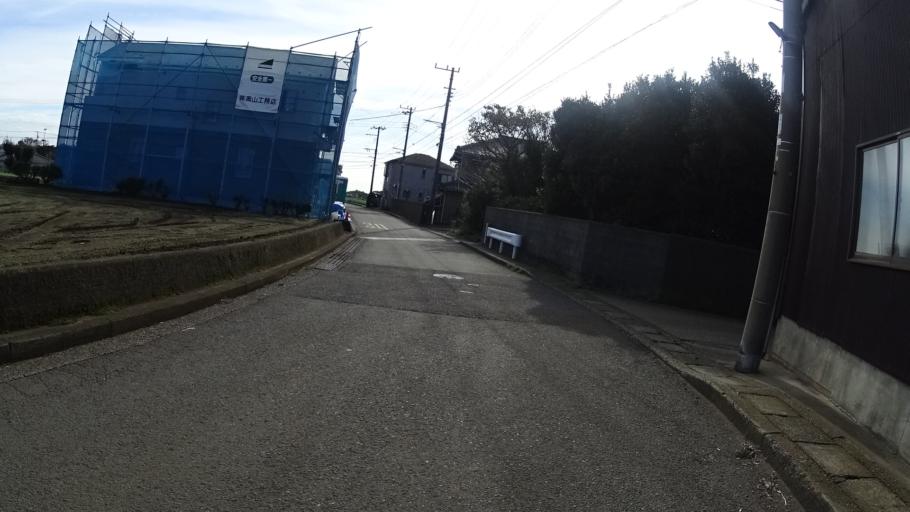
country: JP
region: Kanagawa
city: Miura
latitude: 35.1510
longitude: 139.6712
